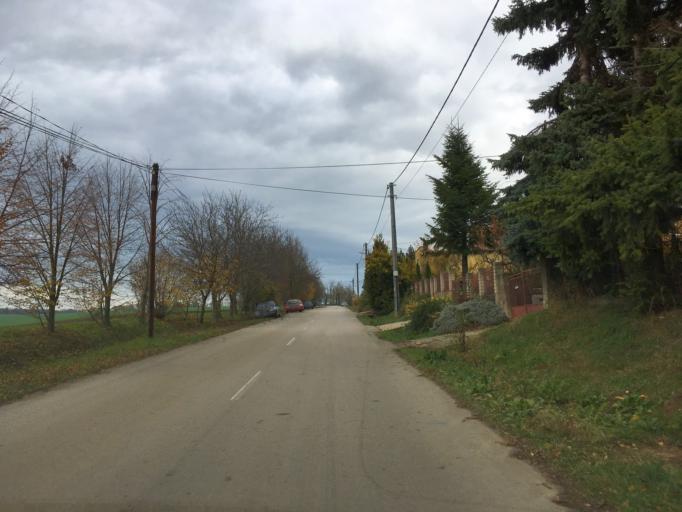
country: SK
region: Nitriansky
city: Svodin
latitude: 48.0210
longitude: 18.4074
